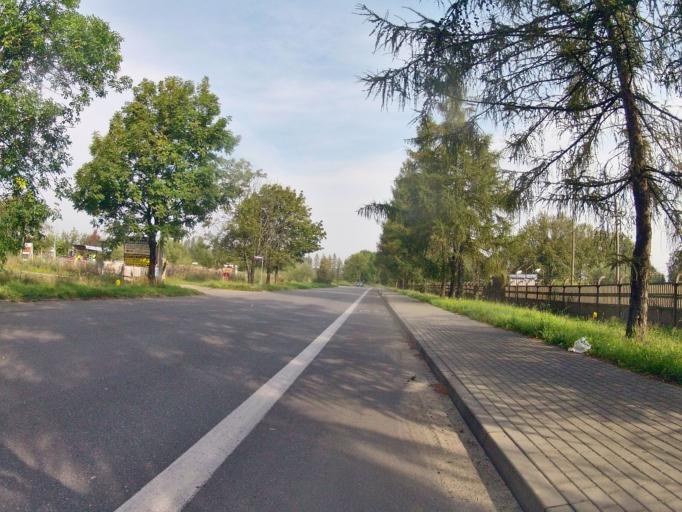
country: PL
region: Subcarpathian Voivodeship
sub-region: Powiat jasielski
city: Jaslo
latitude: 49.7230
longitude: 21.4498
